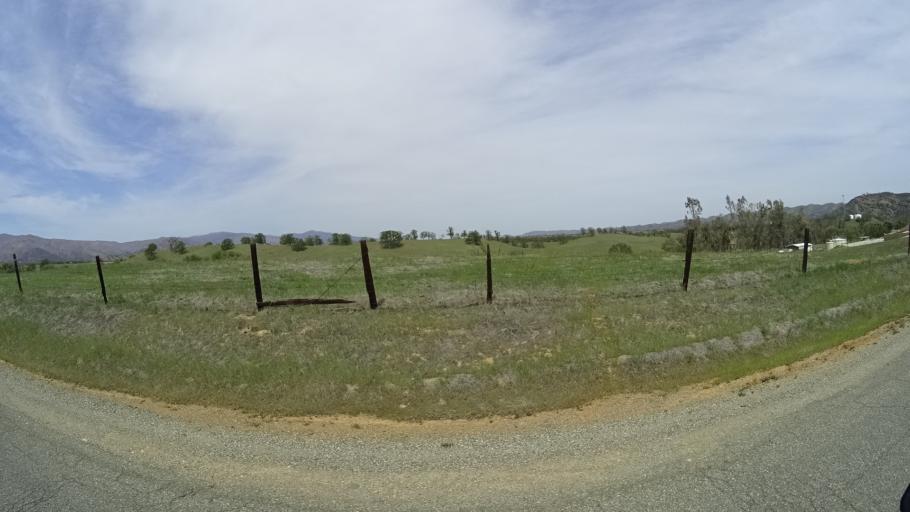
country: US
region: California
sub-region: Glenn County
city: Willows
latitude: 39.5916
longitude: -122.5566
